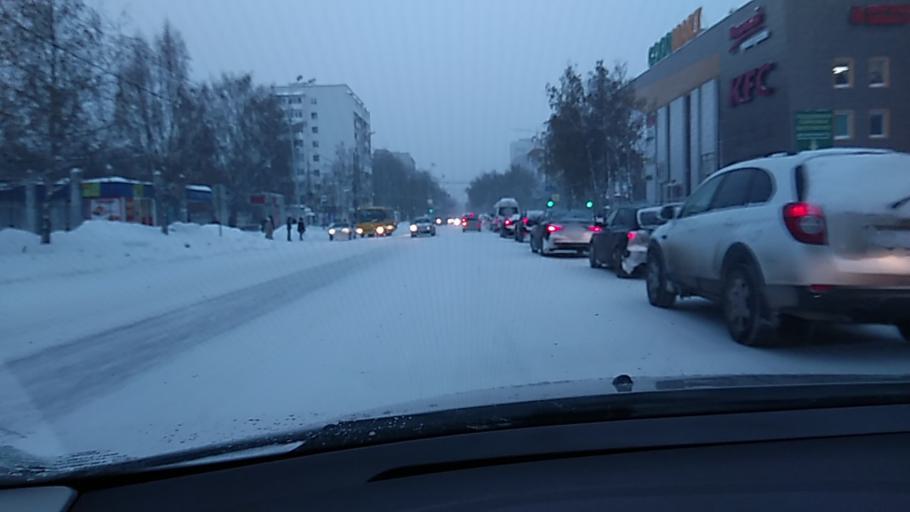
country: RU
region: Sverdlovsk
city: Sovkhoznyy
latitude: 56.8176
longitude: 60.5620
